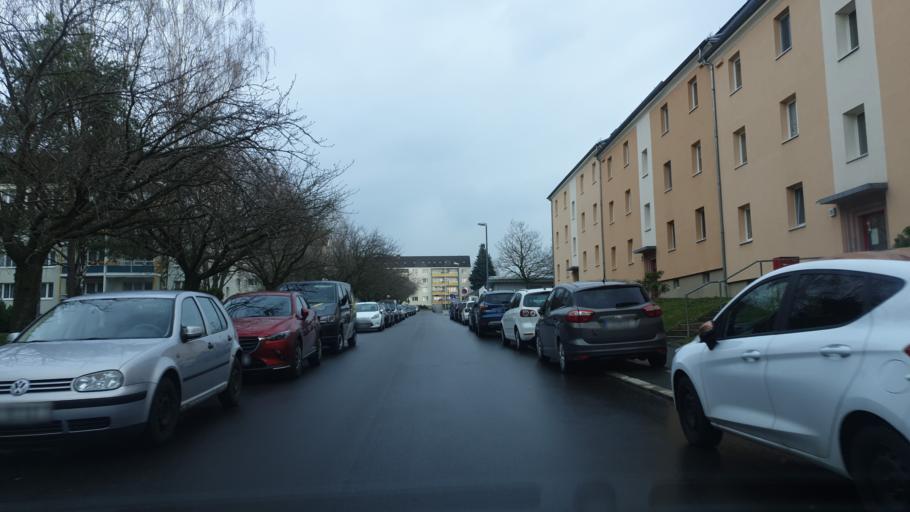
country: DE
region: Saxony
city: Chemnitz
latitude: 50.8114
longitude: 12.9158
